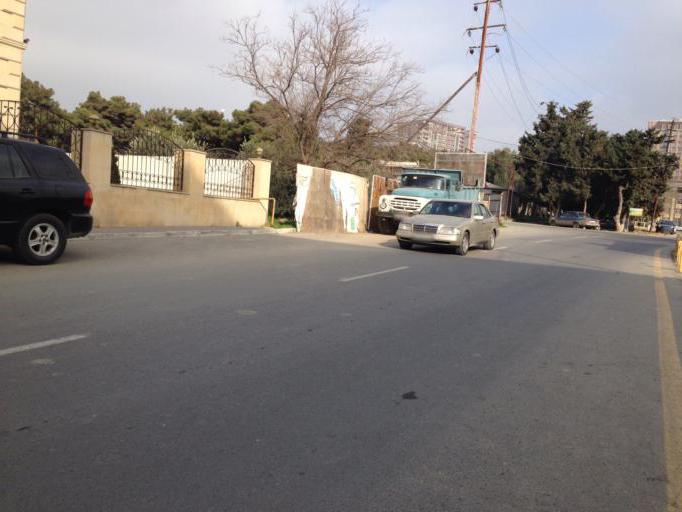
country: AZ
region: Baki
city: Baku
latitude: 40.3943
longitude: 49.8549
